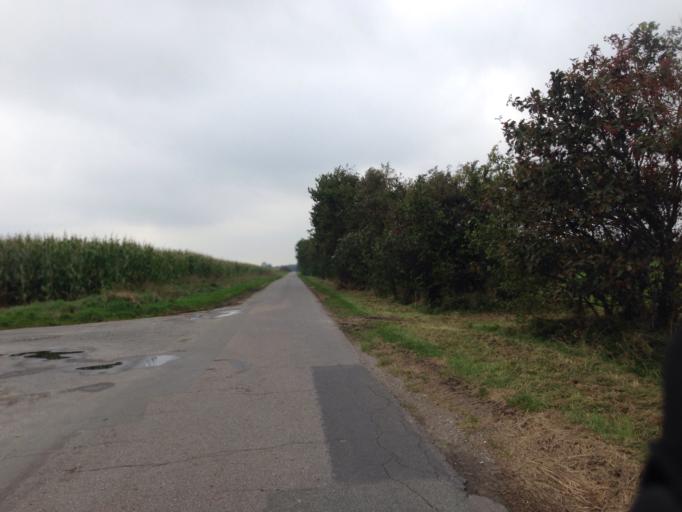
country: DE
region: Schleswig-Holstein
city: Alkersum
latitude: 54.6998
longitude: 8.5067
